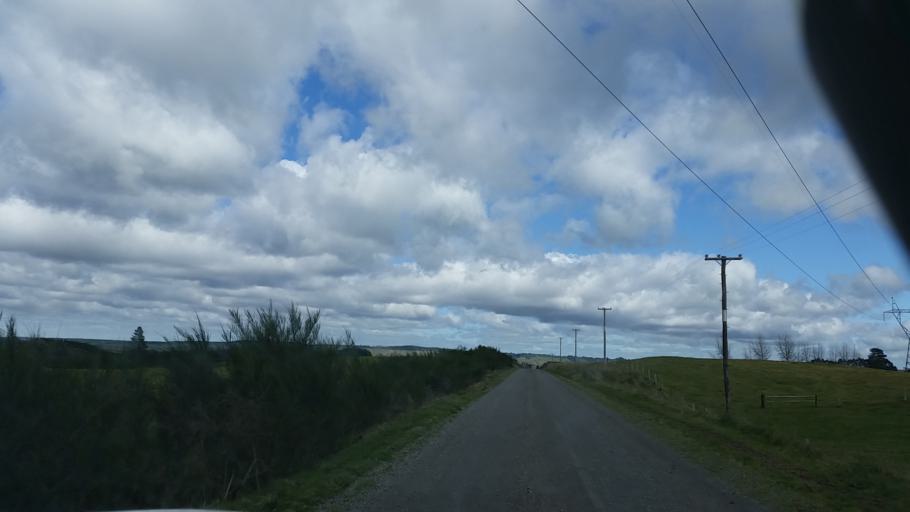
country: NZ
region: Bay of Plenty
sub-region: Whakatane District
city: Murupara
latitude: -38.2970
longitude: 176.5674
